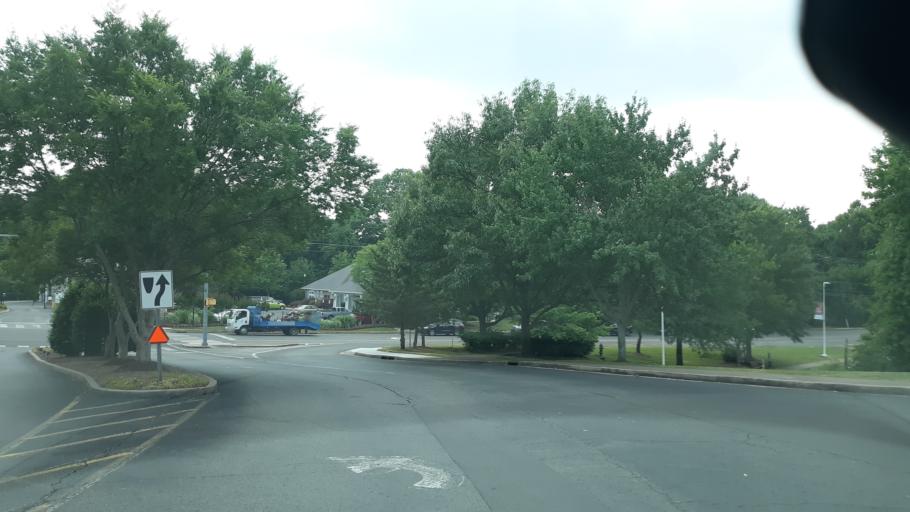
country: US
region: Tennessee
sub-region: Davidson County
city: Lakewood
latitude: 36.1747
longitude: -86.6084
